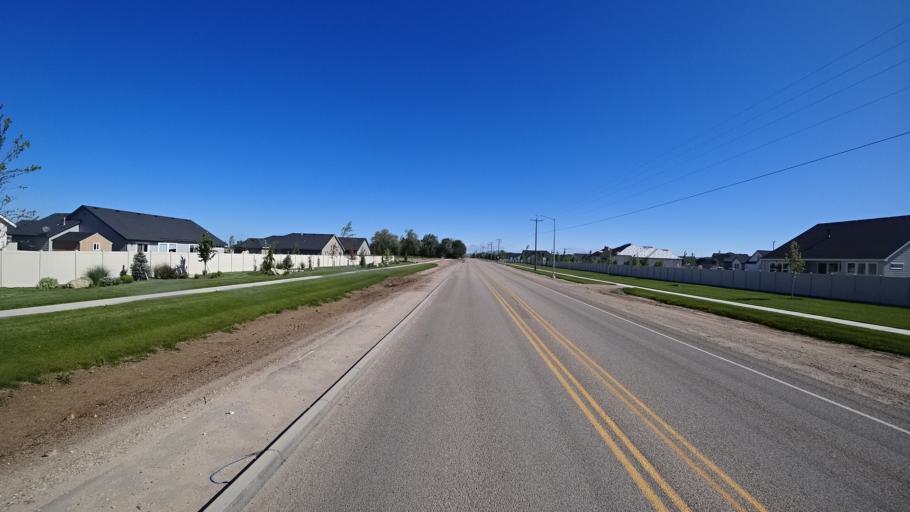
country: US
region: Idaho
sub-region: Ada County
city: Star
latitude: 43.6539
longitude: -116.4537
